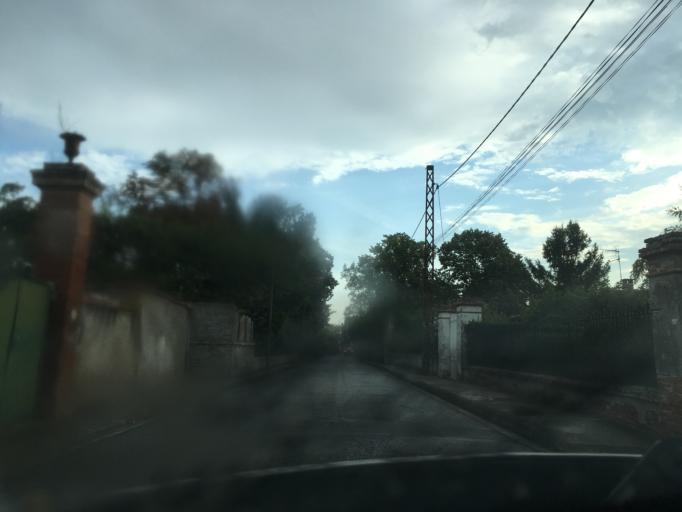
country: FR
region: Midi-Pyrenees
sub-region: Departement de la Haute-Garonne
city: Portet-sur-Garonne
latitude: 43.5619
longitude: 1.3850
